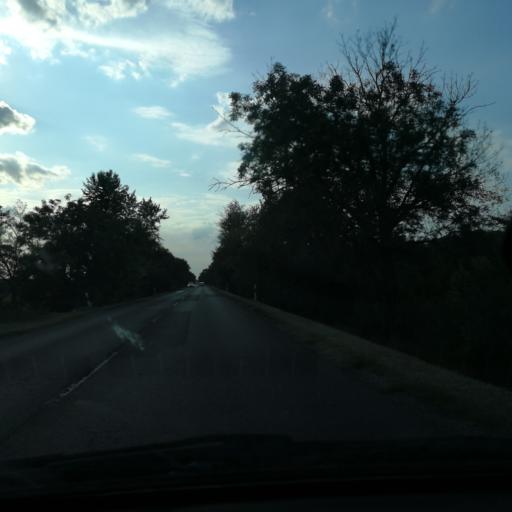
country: HU
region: Csongrad
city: Csongrad
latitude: 46.6903
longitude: 20.1622
